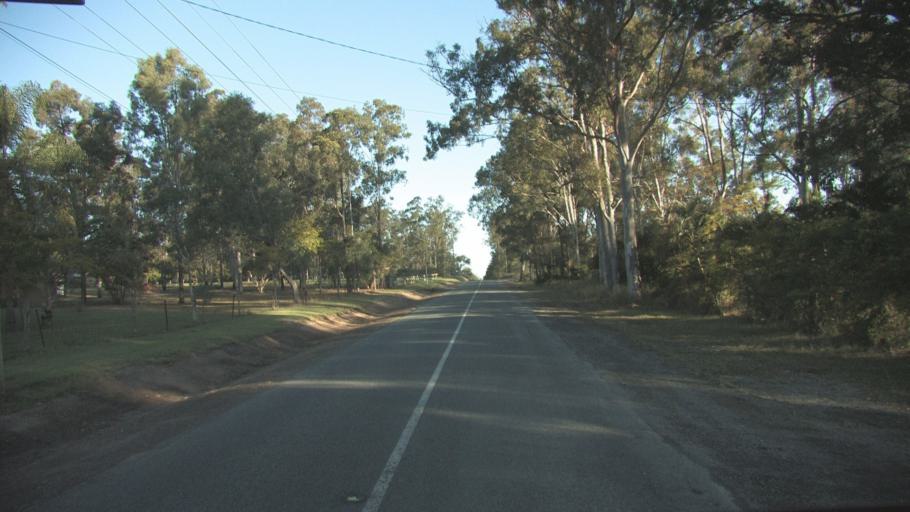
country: AU
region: Queensland
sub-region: Logan
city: Waterford West
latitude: -27.7236
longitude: 153.1476
